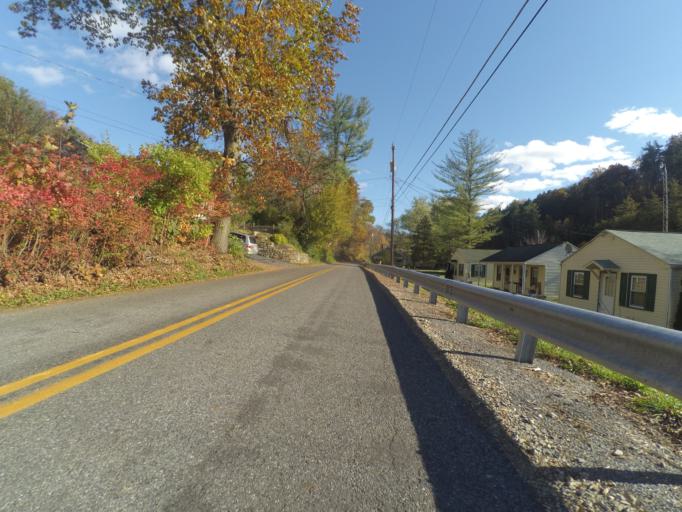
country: US
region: Pennsylvania
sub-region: Centre County
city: Bellefonte
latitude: 40.8880
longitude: -77.7899
